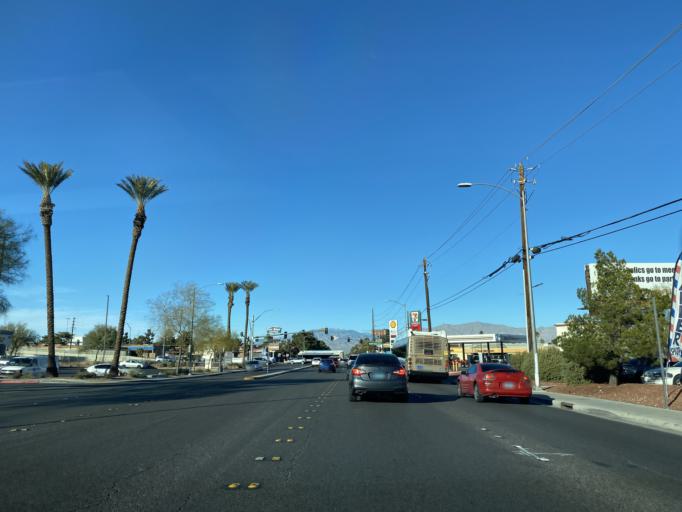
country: US
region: Nevada
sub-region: Clark County
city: Spring Valley
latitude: 36.2021
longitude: -115.2422
